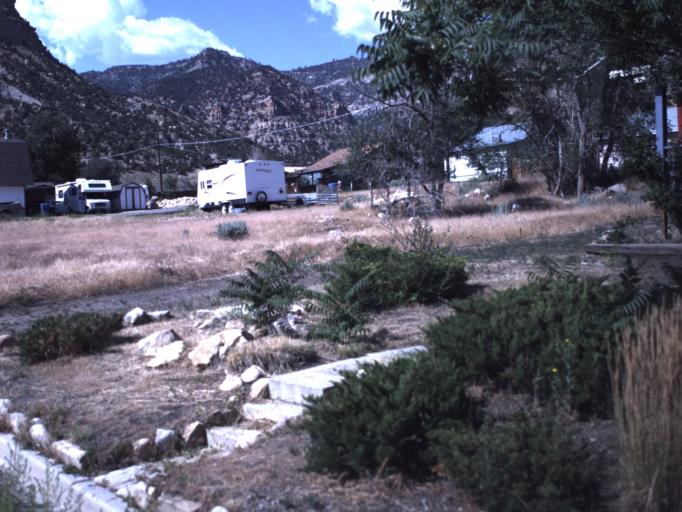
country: US
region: Utah
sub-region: Carbon County
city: Helper
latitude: 39.6868
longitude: -110.8041
